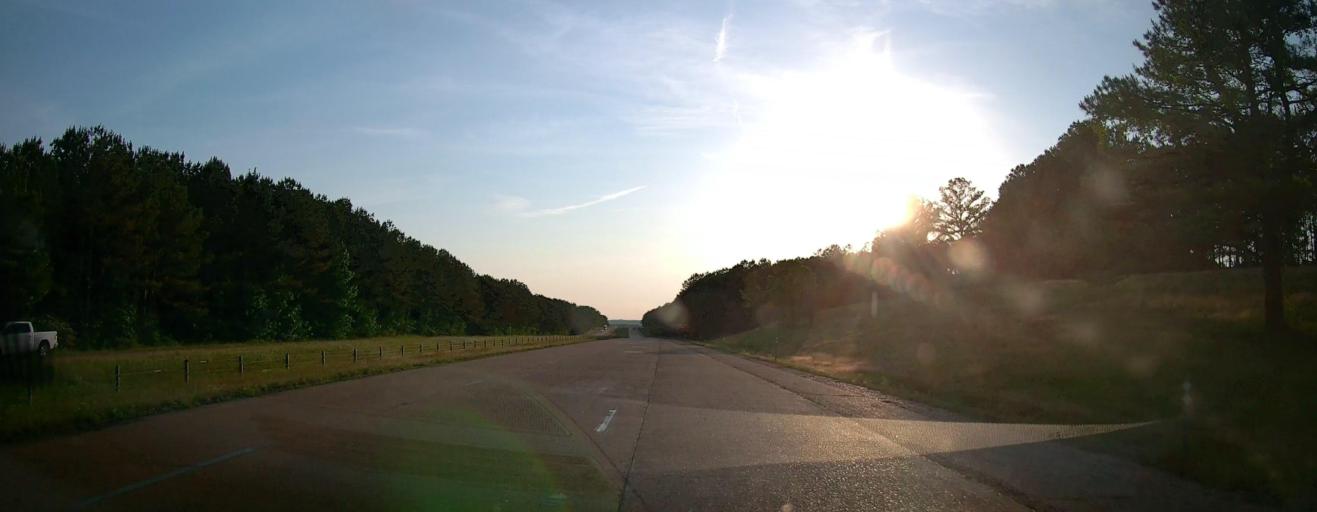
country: US
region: Mississippi
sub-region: Itawamba County
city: Fulton
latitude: 34.2207
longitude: -88.2398
